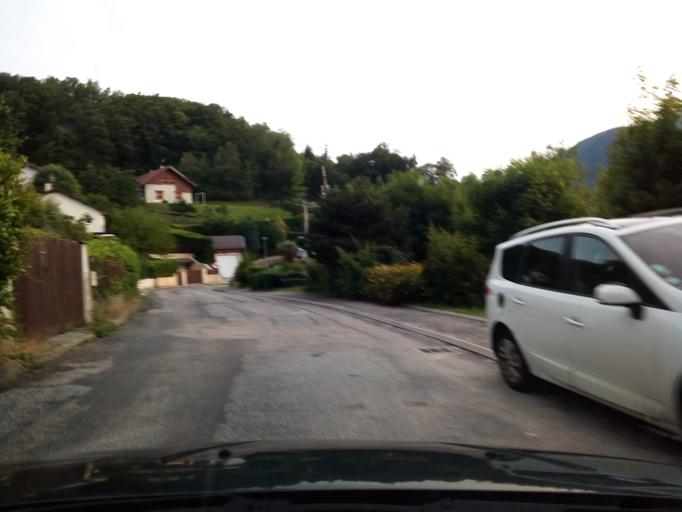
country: FR
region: Rhone-Alpes
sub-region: Departement de l'Isere
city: Saint-Georges-de-Commiers
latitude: 45.0442
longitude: 5.7089
